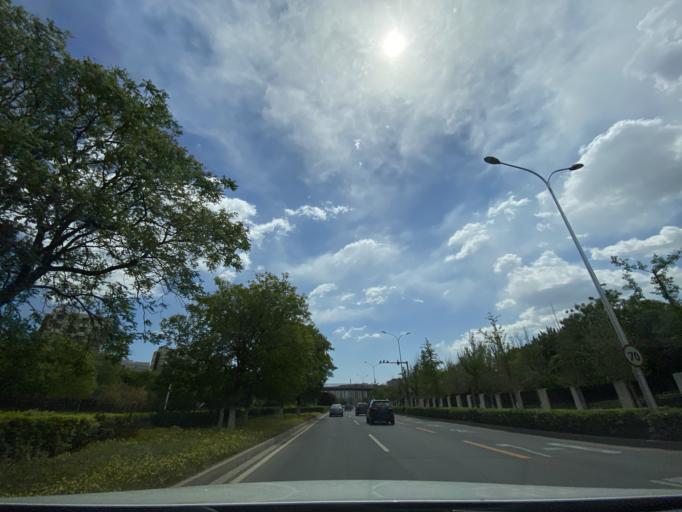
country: CN
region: Beijing
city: Sijiqing
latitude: 39.9360
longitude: 116.2429
